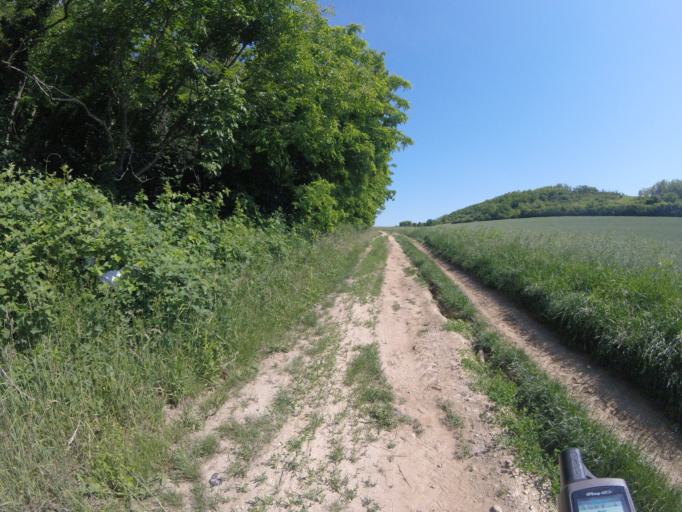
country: HU
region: Zala
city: Zalaszentgrot
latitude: 46.9085
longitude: 17.0546
